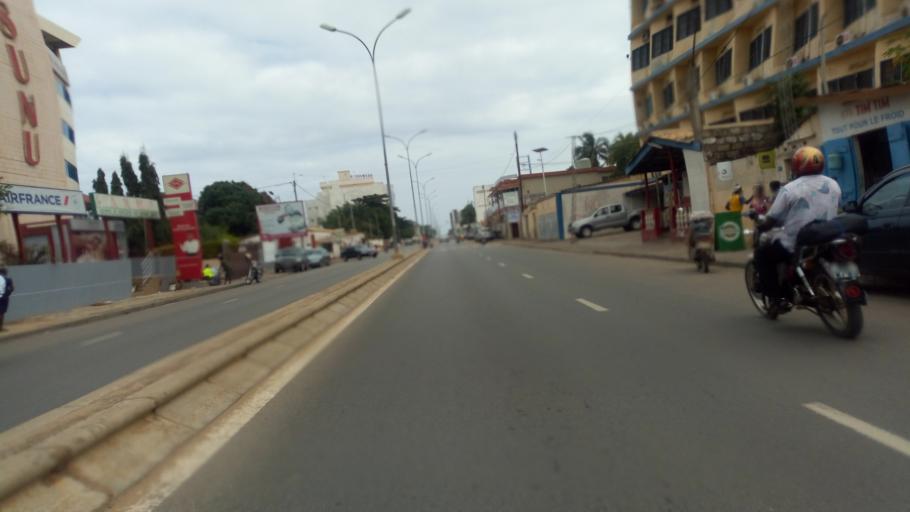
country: TG
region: Maritime
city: Lome
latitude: 6.1254
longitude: 1.2094
